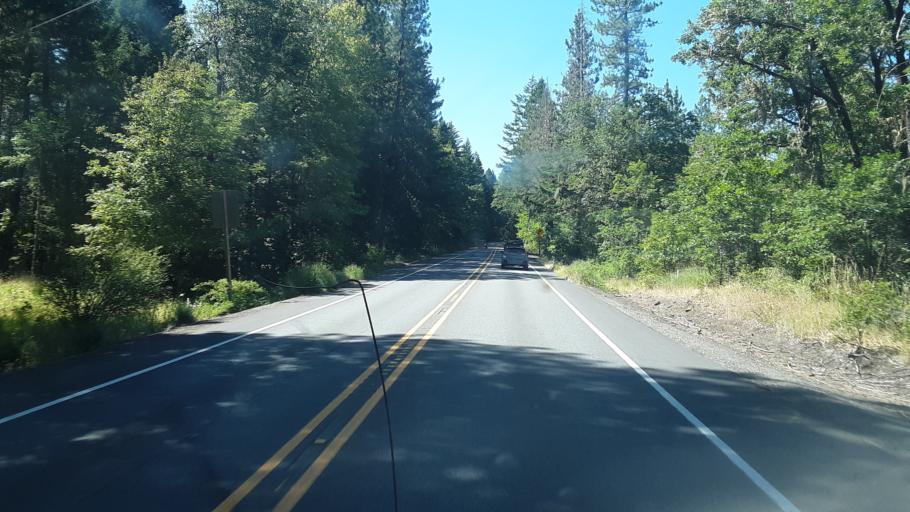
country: US
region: Oregon
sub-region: Josephine County
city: Cave Junction
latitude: 42.2599
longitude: -123.6187
